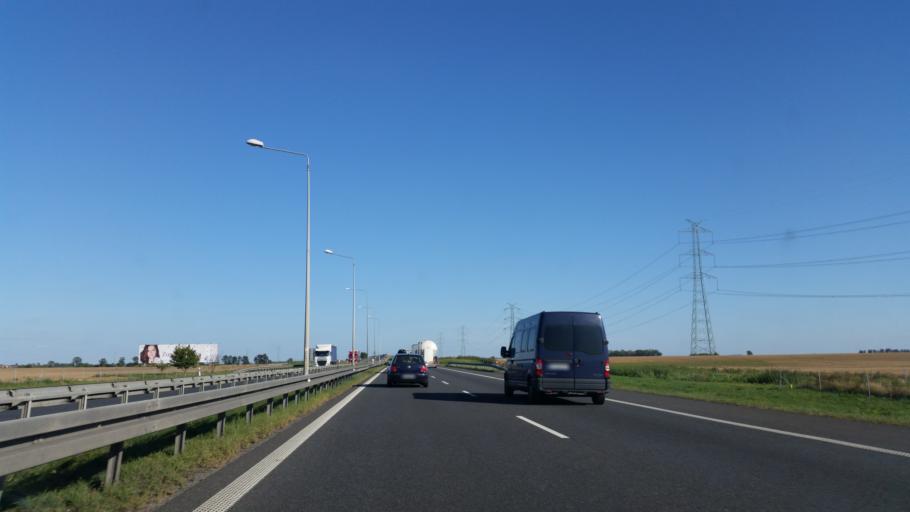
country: PL
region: Opole Voivodeship
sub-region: Powiat brzeski
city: Olszanka
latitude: 50.7536
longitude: 17.4363
